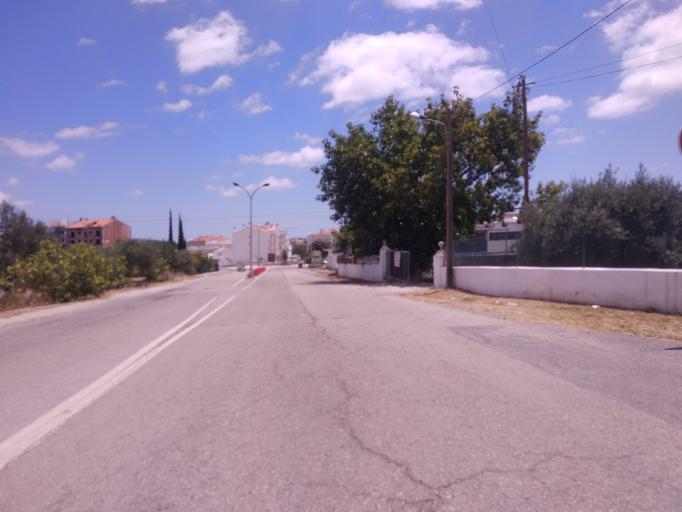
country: PT
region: Faro
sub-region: Sao Bras de Alportel
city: Sao Bras de Alportel
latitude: 37.1605
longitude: -7.8904
